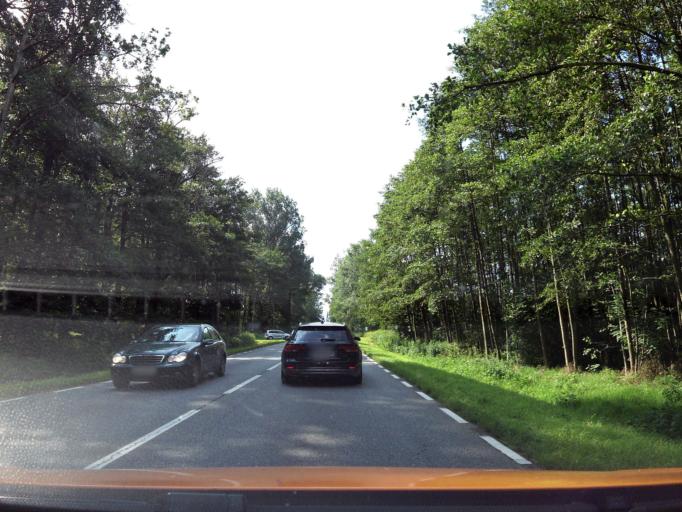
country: PL
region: West Pomeranian Voivodeship
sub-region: Powiat gryficki
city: Ploty
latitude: 53.8129
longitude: 15.2768
